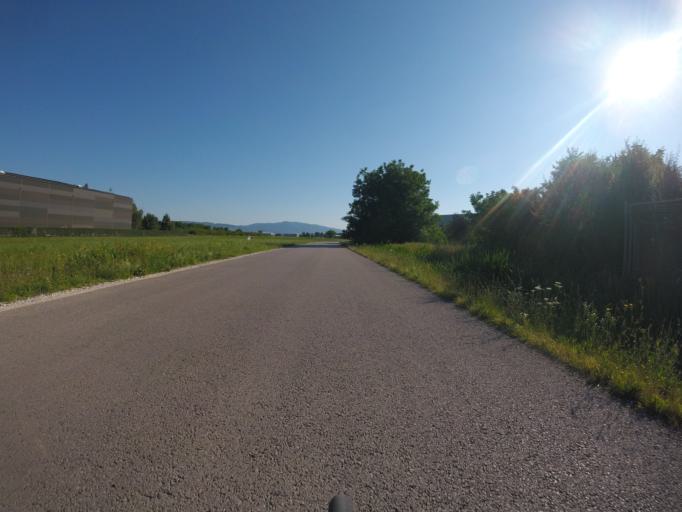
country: HR
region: Grad Zagreb
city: Lucko
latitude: 45.7461
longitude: 15.8707
